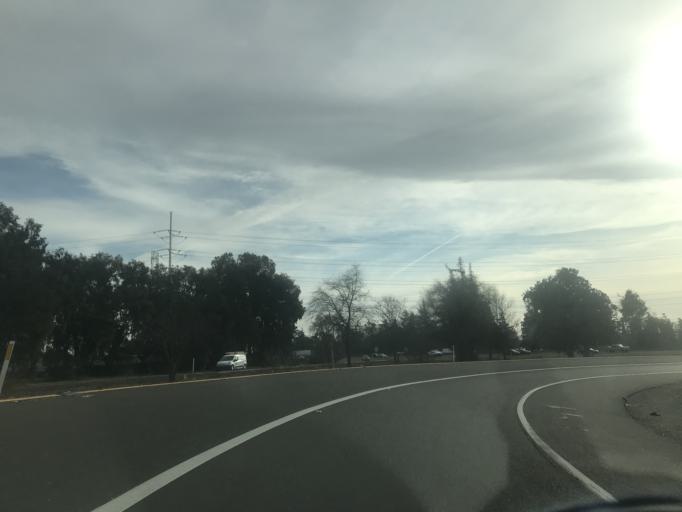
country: US
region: California
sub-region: Sacramento County
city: Parkway
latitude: 38.5097
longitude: -121.4578
